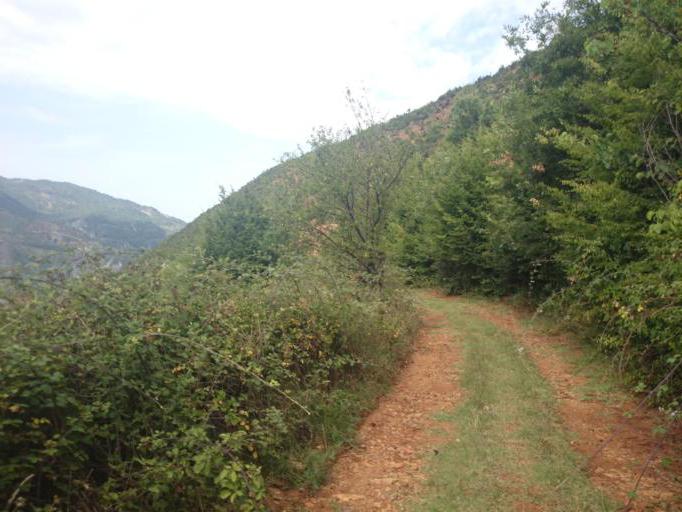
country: AL
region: Elbasan
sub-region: Rrethi i Gramshit
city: Kodovjat
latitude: 40.7734
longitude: 20.3153
